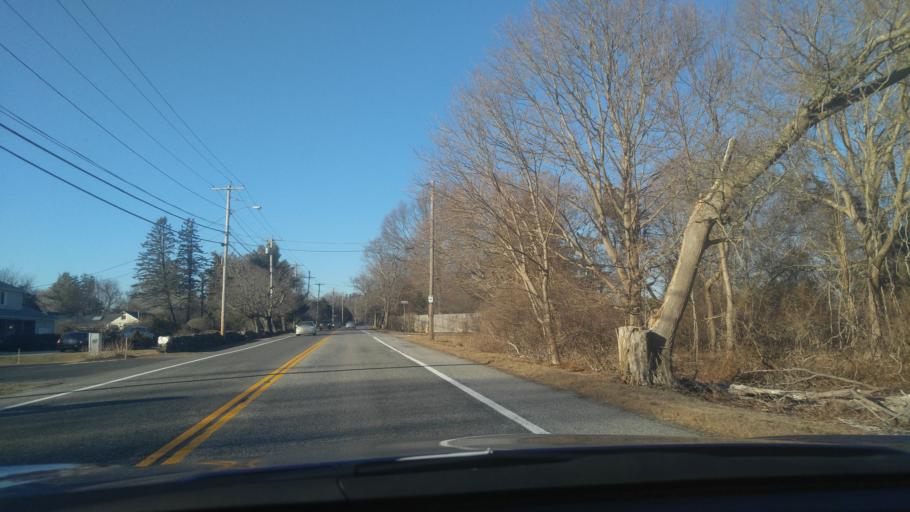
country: US
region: Rhode Island
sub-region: Washington County
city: Narragansett Pier
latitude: 41.4671
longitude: -71.4335
